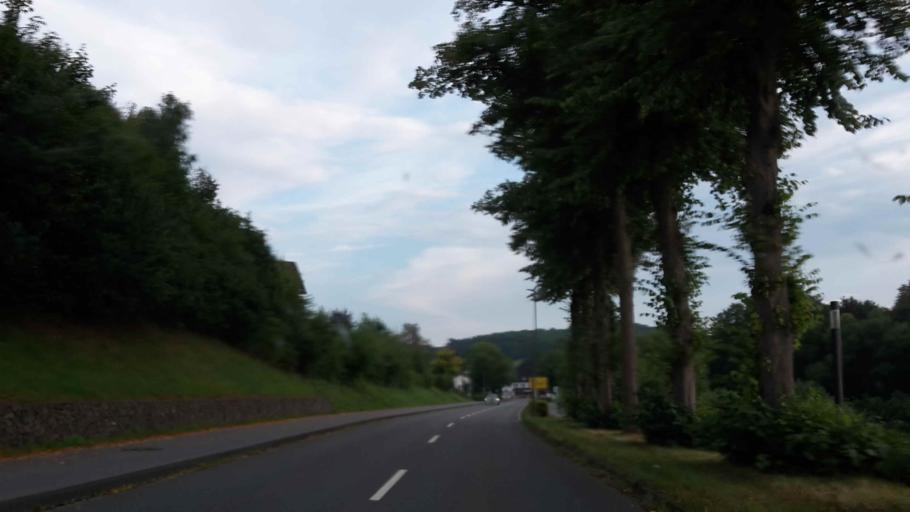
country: DE
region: North Rhine-Westphalia
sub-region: Regierungsbezirk Arnsberg
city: Sundern
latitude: 51.3023
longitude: 7.9496
